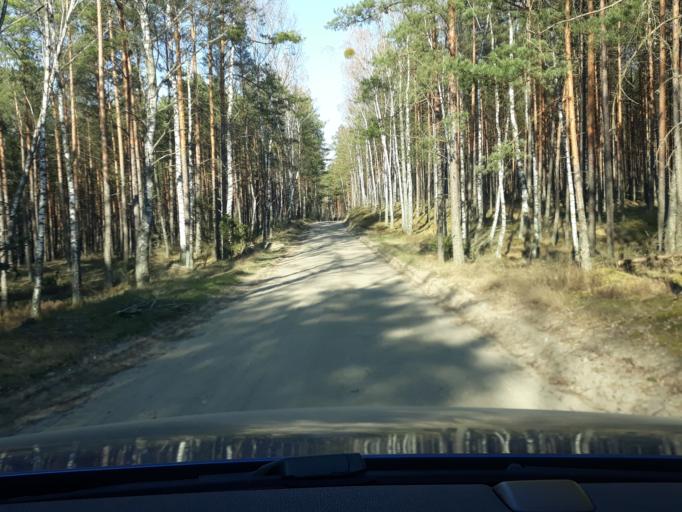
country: PL
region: Pomeranian Voivodeship
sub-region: Powiat bytowski
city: Lipnica
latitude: 53.9073
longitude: 17.4244
